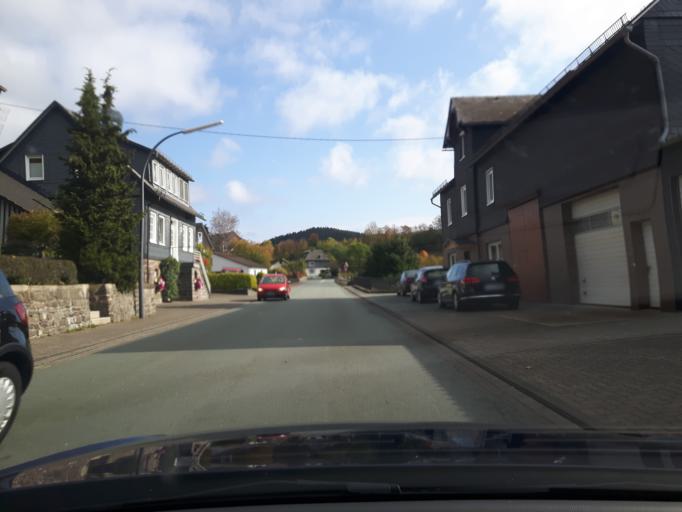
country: DE
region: North Rhine-Westphalia
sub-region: Regierungsbezirk Arnsberg
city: Bad Berleburg
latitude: 51.0129
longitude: 8.4315
